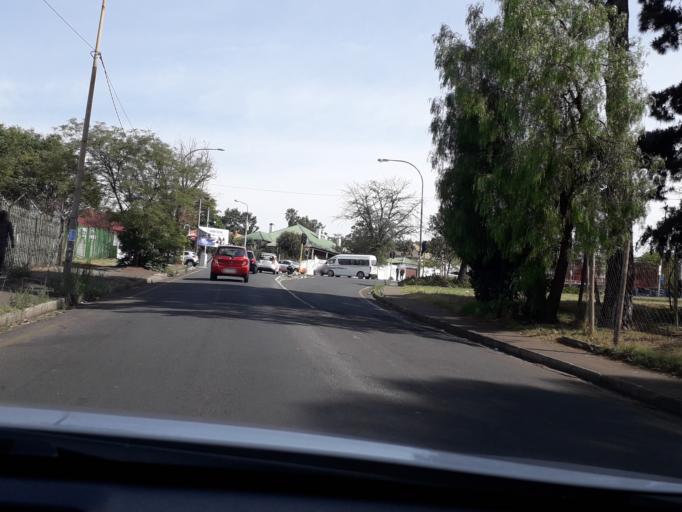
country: ZA
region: Gauteng
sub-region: City of Johannesburg Metropolitan Municipality
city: Johannesburg
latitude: -26.1949
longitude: 28.0056
